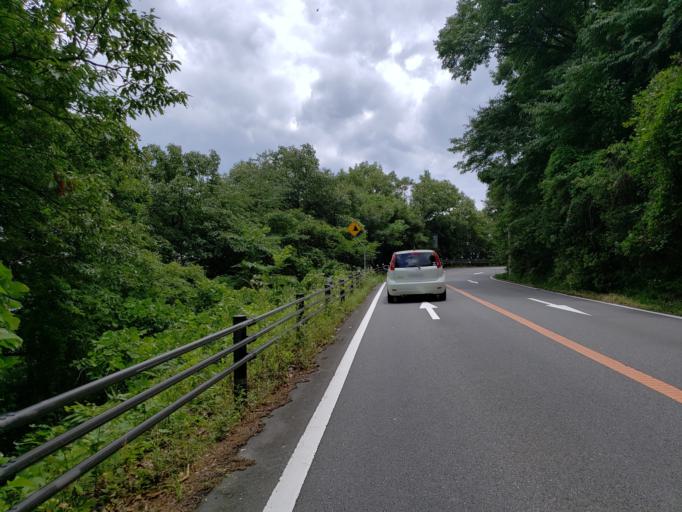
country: JP
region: Hyogo
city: Aioi
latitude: 34.7680
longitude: 134.4915
